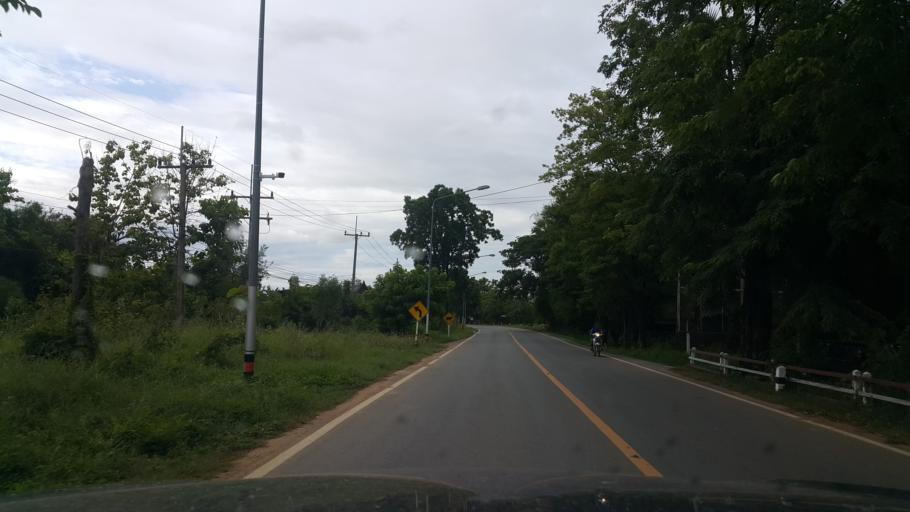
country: TH
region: Sukhothai
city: Ban Na
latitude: 17.0365
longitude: 99.7035
